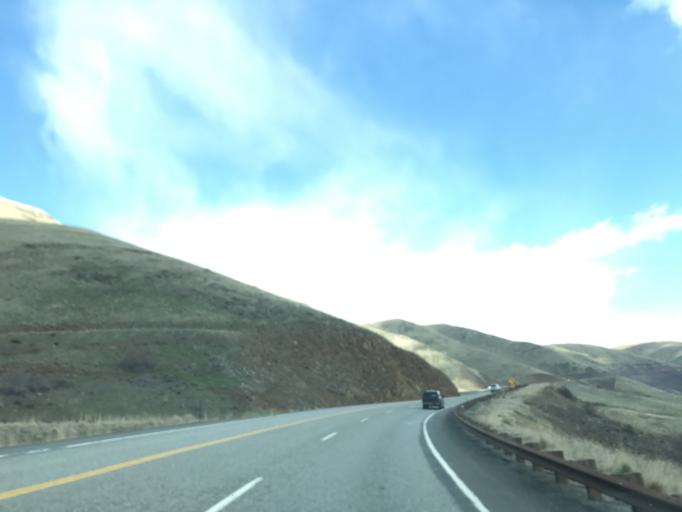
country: US
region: Idaho
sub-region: Idaho County
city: Grangeville
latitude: 45.7908
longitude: -116.2915
